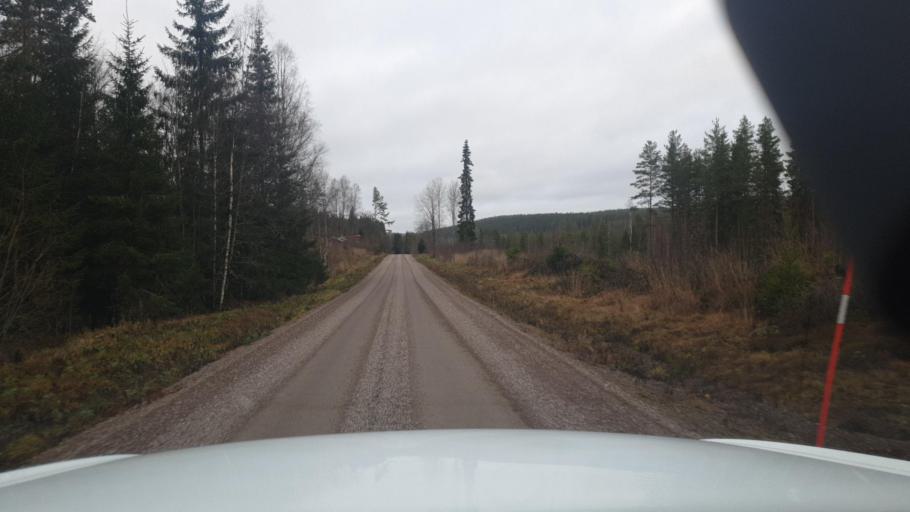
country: SE
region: Vaermland
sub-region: Eda Kommun
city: Charlottenberg
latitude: 60.0779
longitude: 12.5250
